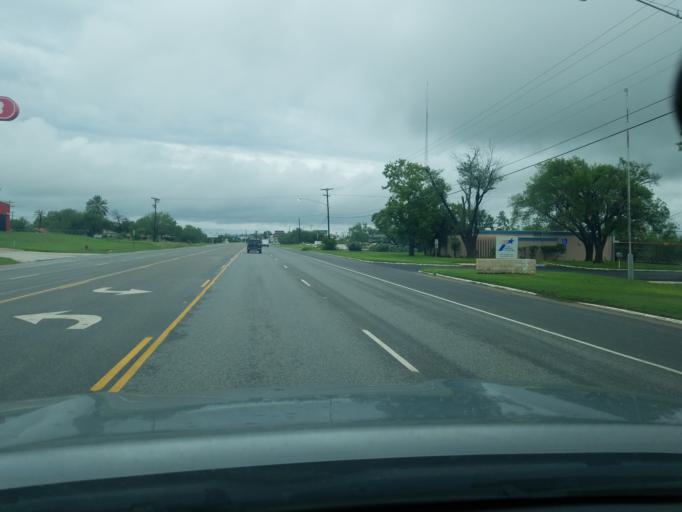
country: US
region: Texas
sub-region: Dimmit County
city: Carrizo Springs
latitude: 28.5360
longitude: -99.8509
